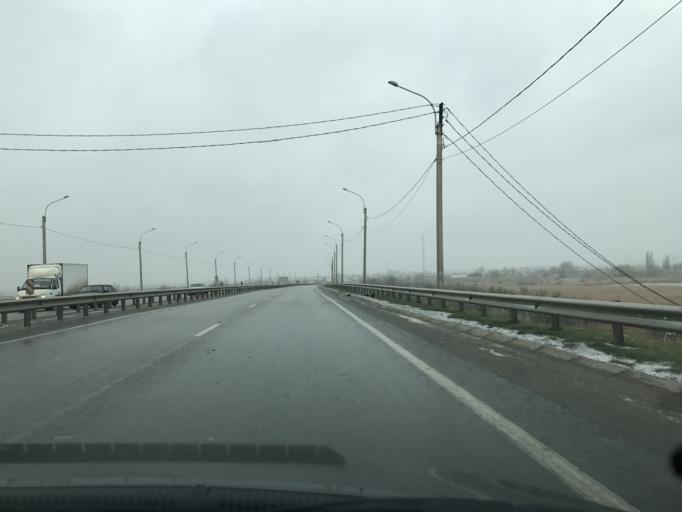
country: RU
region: Rostov
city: Bataysk
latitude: 47.1640
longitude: 39.7591
